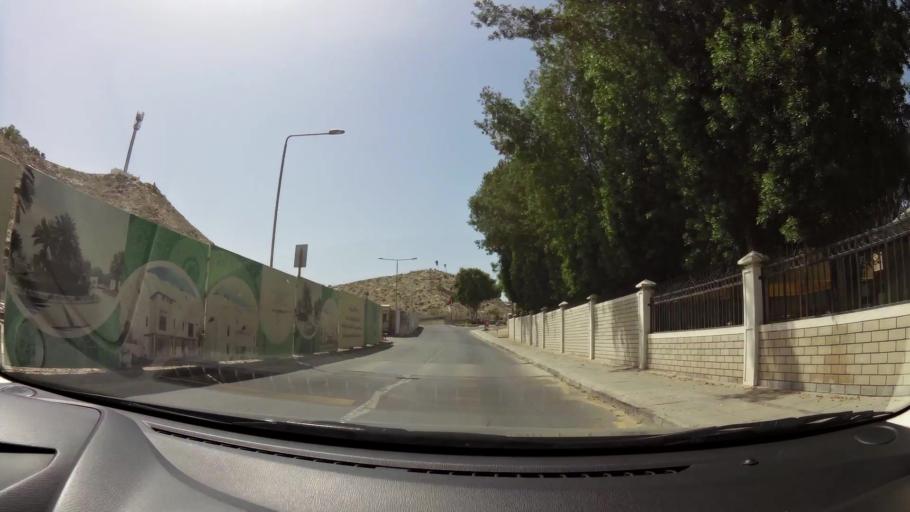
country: OM
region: Muhafazat Masqat
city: Muscat
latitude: 23.6395
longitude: 58.4973
